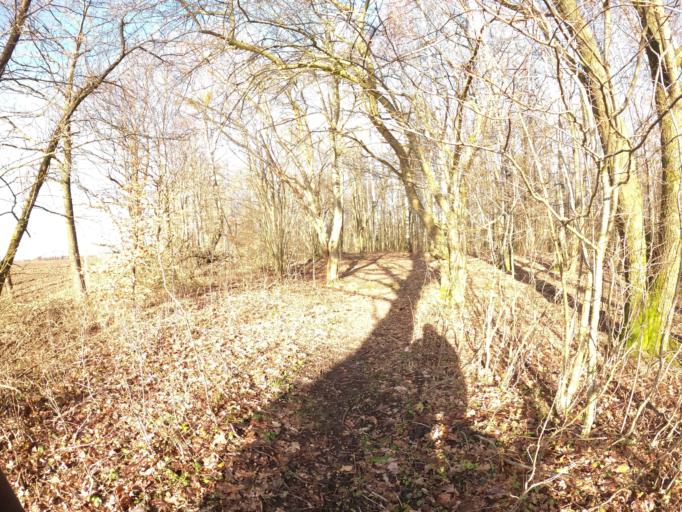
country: PL
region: West Pomeranian Voivodeship
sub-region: Powiat koszalinski
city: Polanow
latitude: 54.1469
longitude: 16.7665
